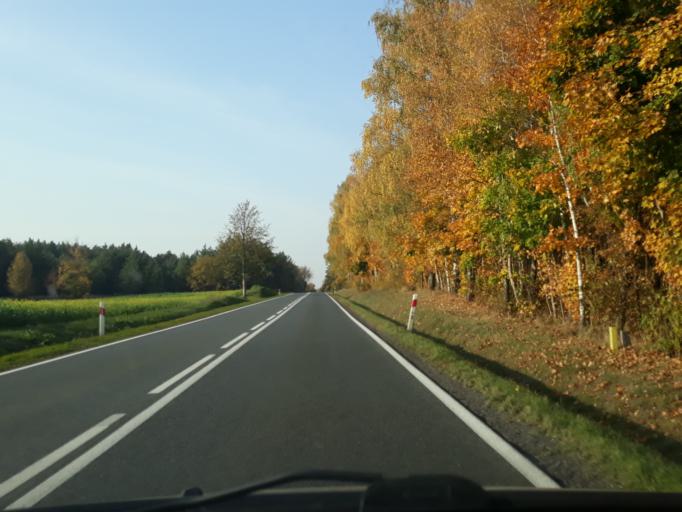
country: PL
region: Kujawsko-Pomorskie
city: Kamien Krajenski
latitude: 53.5442
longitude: 17.5132
